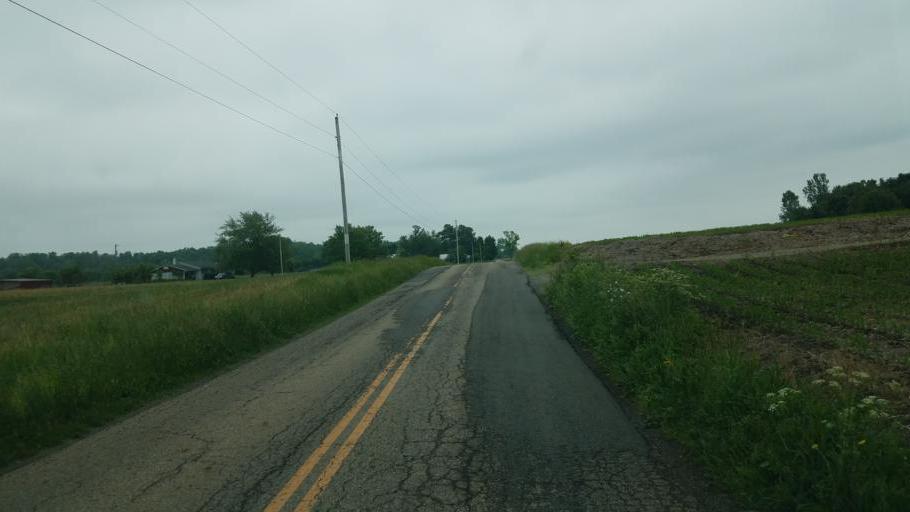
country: US
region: Ohio
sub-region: Knox County
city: Centerburg
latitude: 40.3376
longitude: -82.7265
